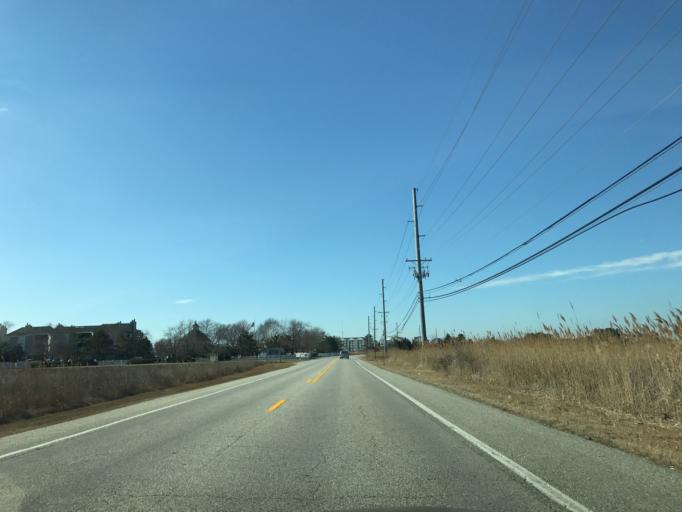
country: US
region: Maryland
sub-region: Queen Anne's County
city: Grasonville
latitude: 38.9658
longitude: -76.2331
